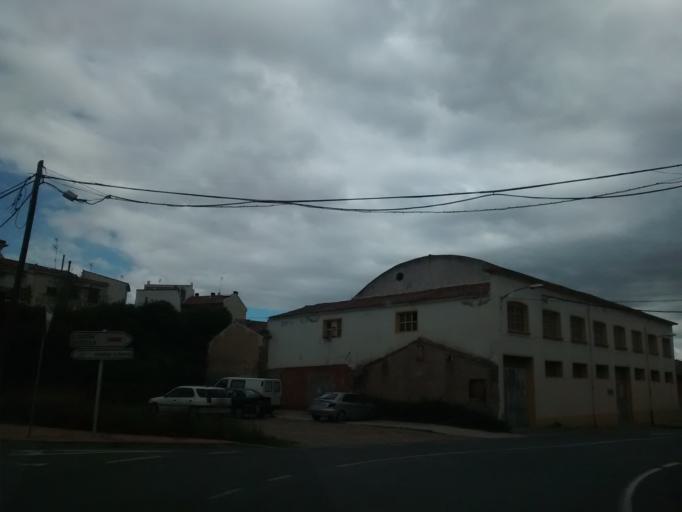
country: ES
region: La Rioja
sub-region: Provincia de La Rioja
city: Pradejon
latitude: 42.3194
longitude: -2.0926
